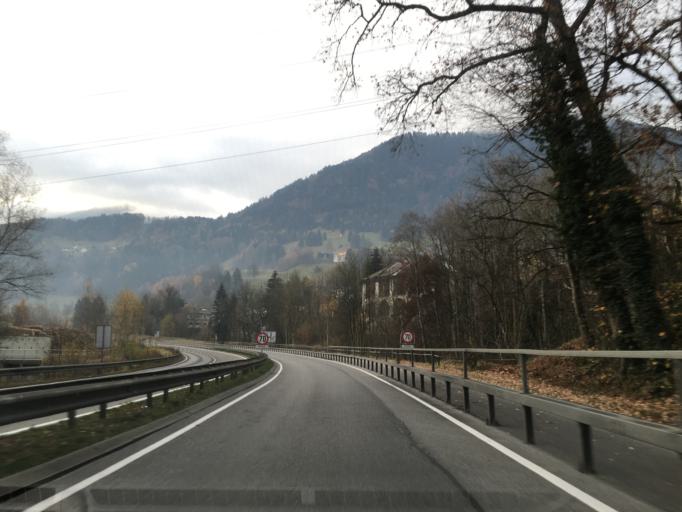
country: AT
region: Vorarlberg
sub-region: Politischer Bezirk Feldkirch
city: Feldkirch
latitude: 47.2288
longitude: 9.6041
